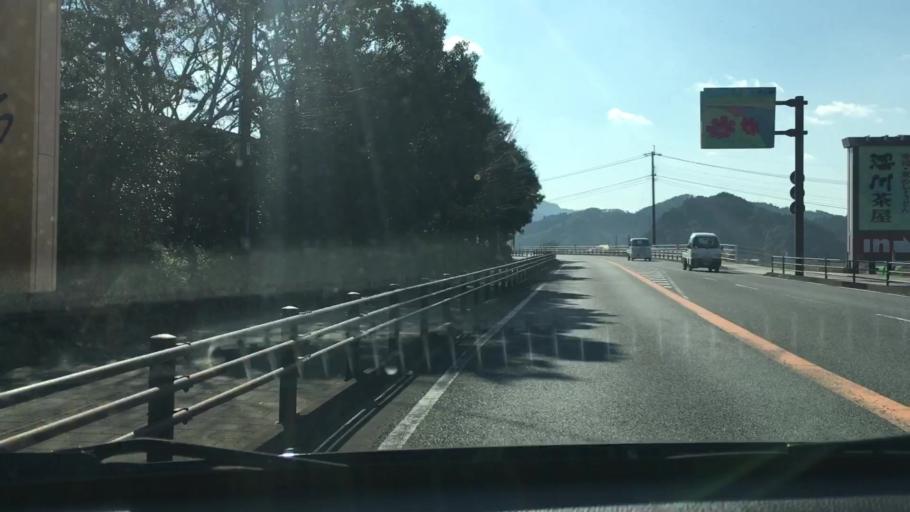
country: JP
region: Oita
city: Saiki
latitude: 32.9642
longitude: 131.8380
